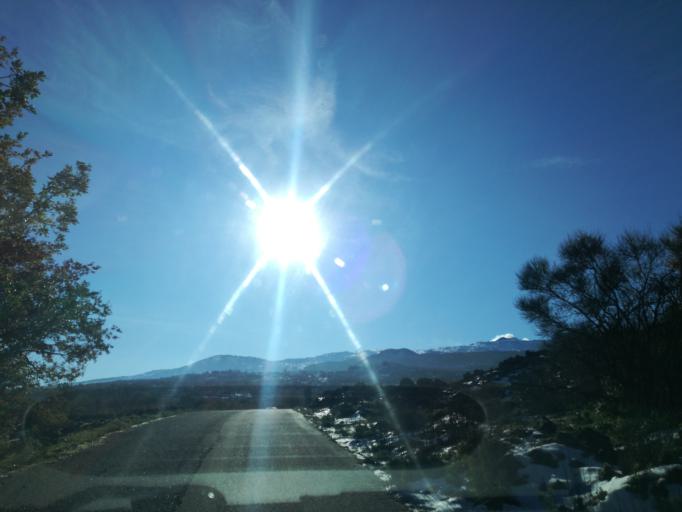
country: IT
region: Sicily
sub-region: Catania
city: Randazzo
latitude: 37.8590
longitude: 14.9814
